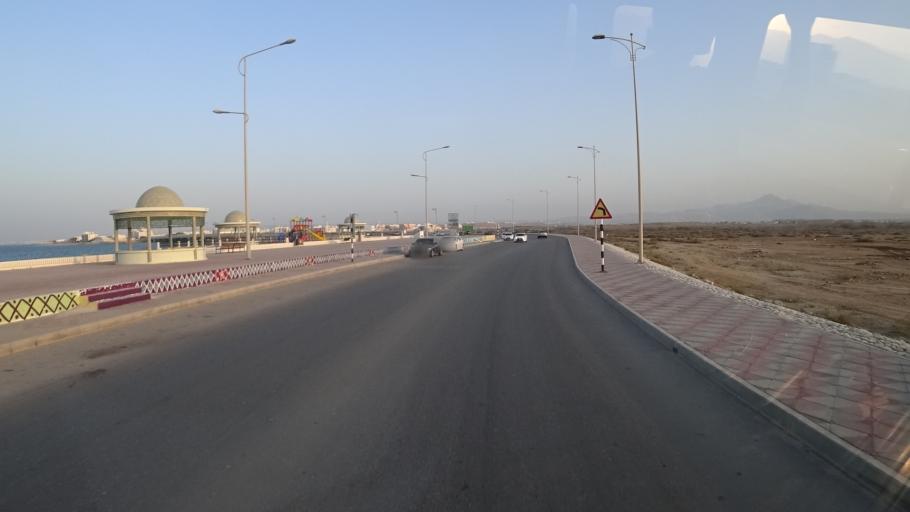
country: OM
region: Ash Sharqiyah
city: Sur
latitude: 22.6009
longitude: 59.4854
